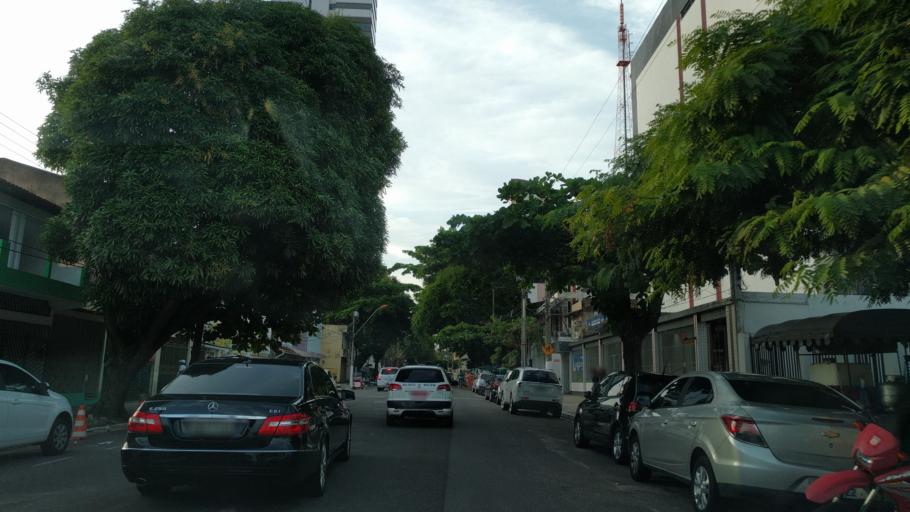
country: BR
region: Para
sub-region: Belem
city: Belem
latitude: -1.4647
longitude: -48.4895
